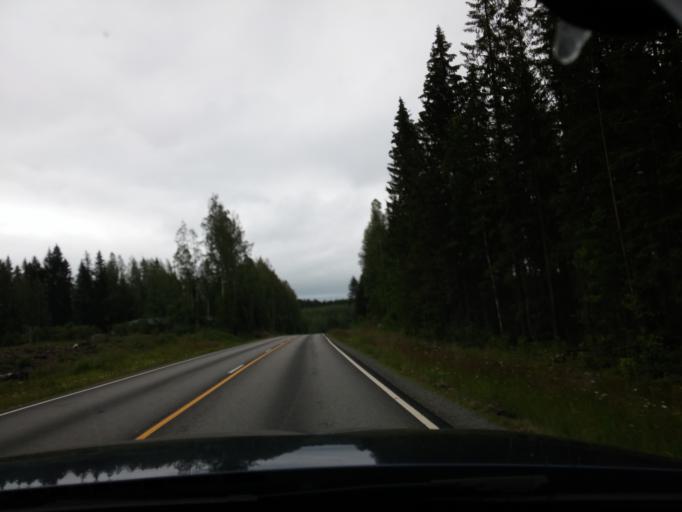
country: FI
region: Central Finland
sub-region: Saarijaervi-Viitasaari
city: Saarijaervi
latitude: 62.6818
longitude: 25.2364
